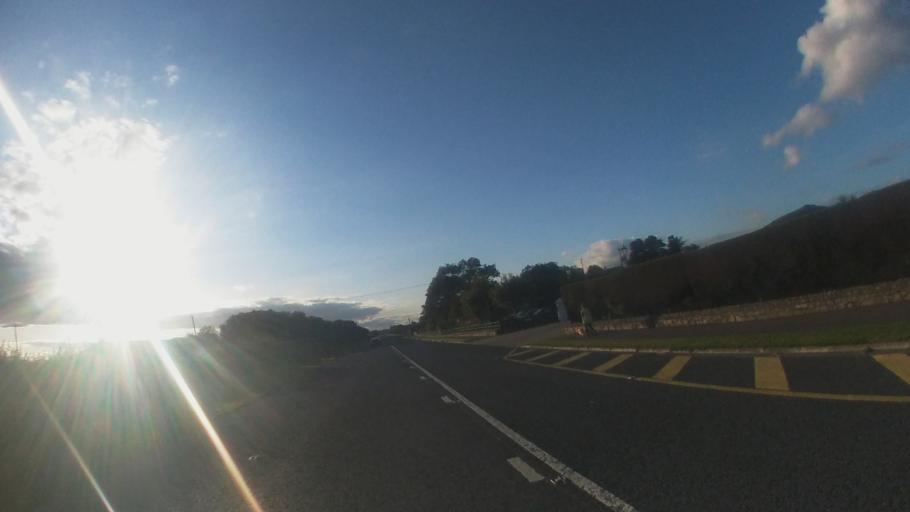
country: IE
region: Leinster
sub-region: Lu
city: Blackrock
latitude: 54.0076
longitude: -6.2913
